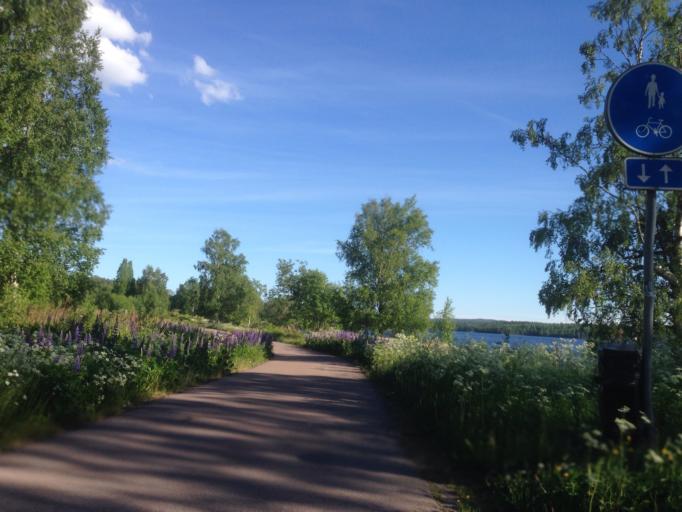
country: SE
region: Dalarna
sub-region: Ludvika Kommun
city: Ludvika
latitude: 60.1107
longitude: 15.2081
